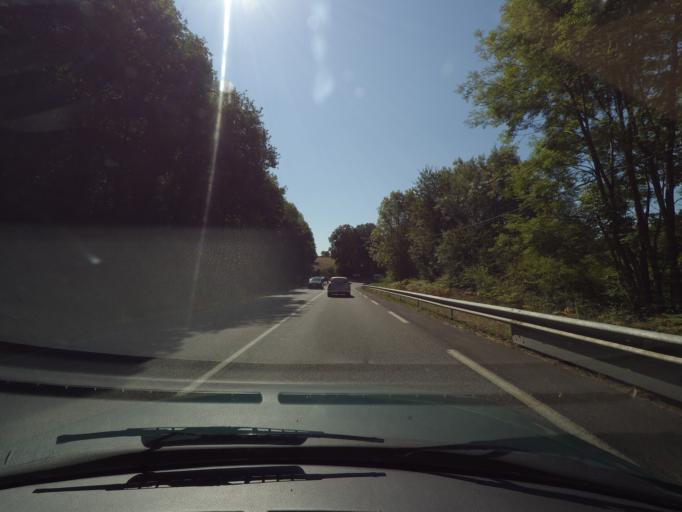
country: FR
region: Limousin
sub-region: Departement de la Haute-Vienne
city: Bellac
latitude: 46.1008
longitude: 1.0758
